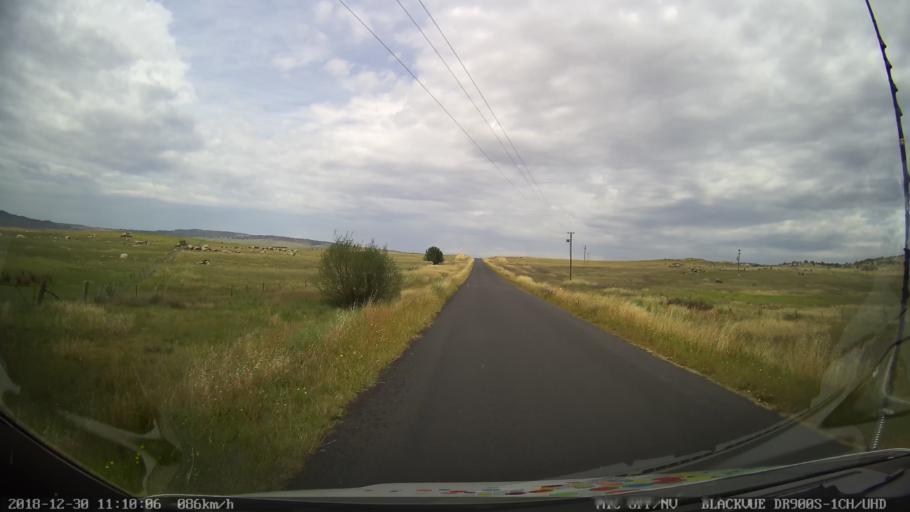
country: AU
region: New South Wales
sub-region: Snowy River
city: Berridale
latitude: -36.5117
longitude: 148.7853
